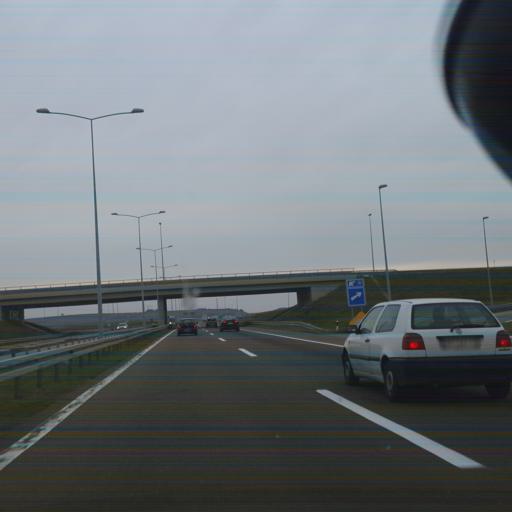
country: RS
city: Beska
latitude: 45.1349
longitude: 20.0880
